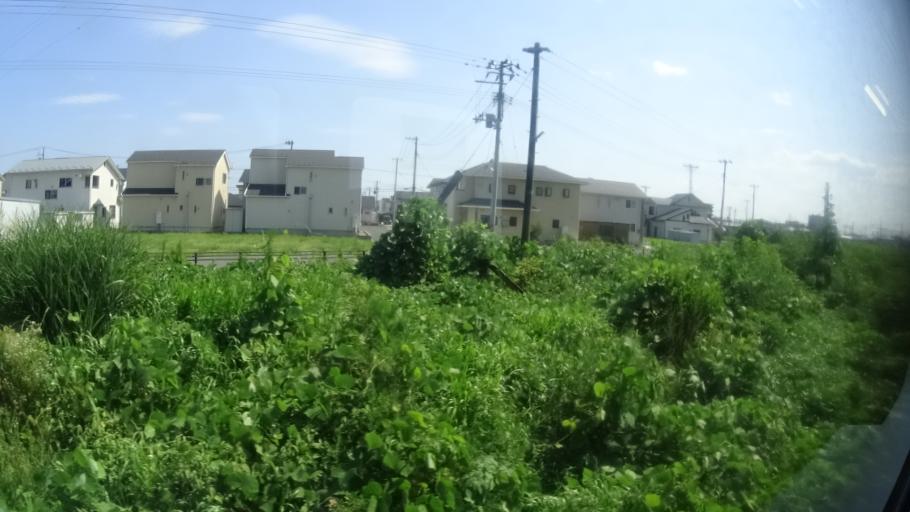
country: JP
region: Miyagi
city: Kogota
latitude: 38.5453
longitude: 141.0663
